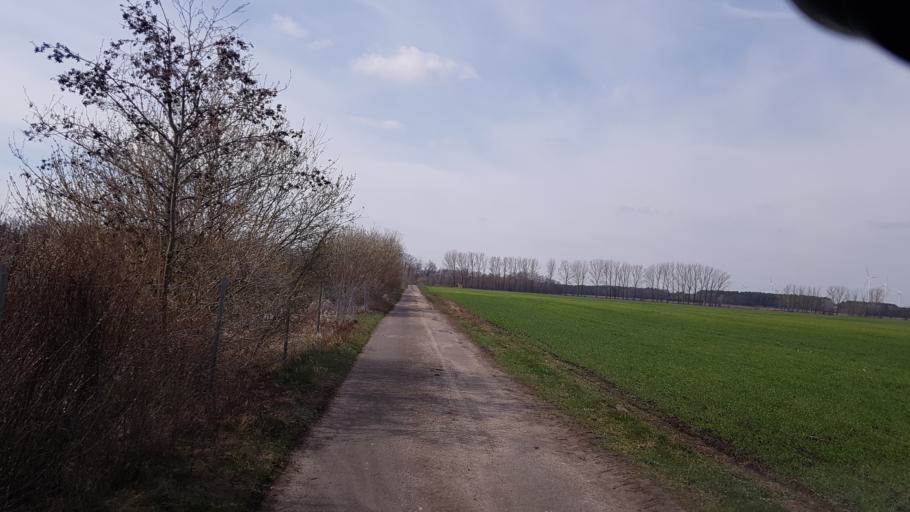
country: DE
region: Brandenburg
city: Bronkow
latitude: 51.6374
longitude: 13.9167
